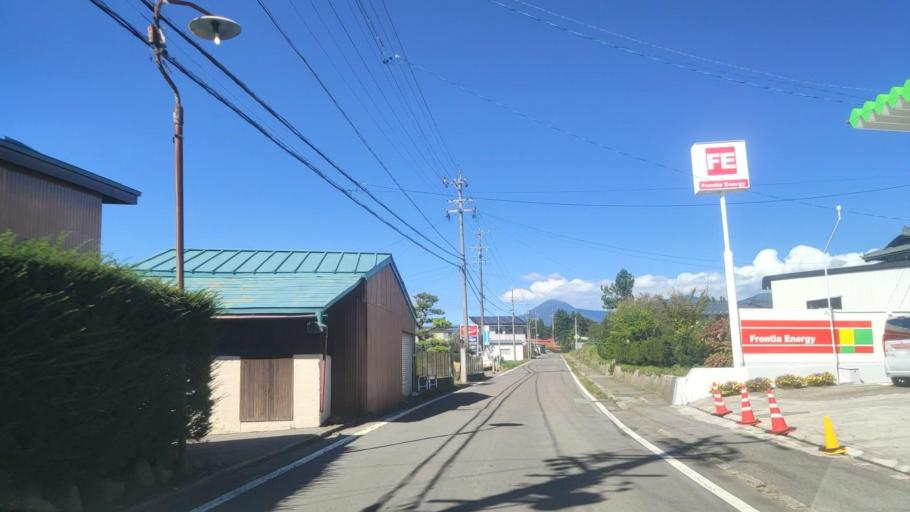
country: JP
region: Nagano
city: Chino
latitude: 35.9702
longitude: 138.2189
